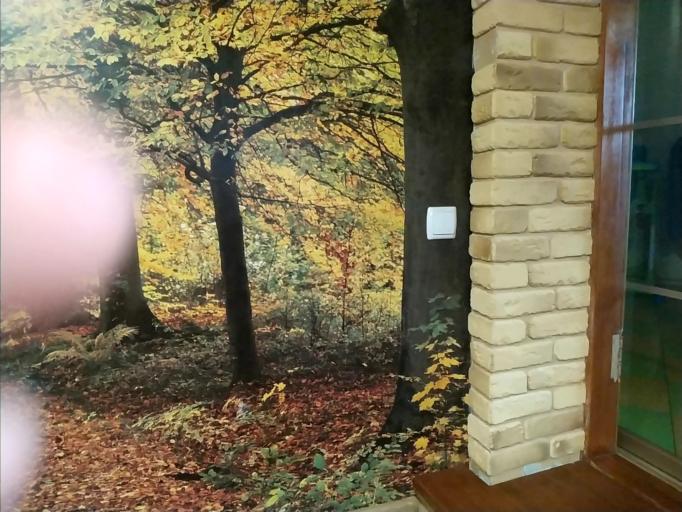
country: RU
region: Smolensk
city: Safonovo
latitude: 55.1919
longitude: 33.1050
